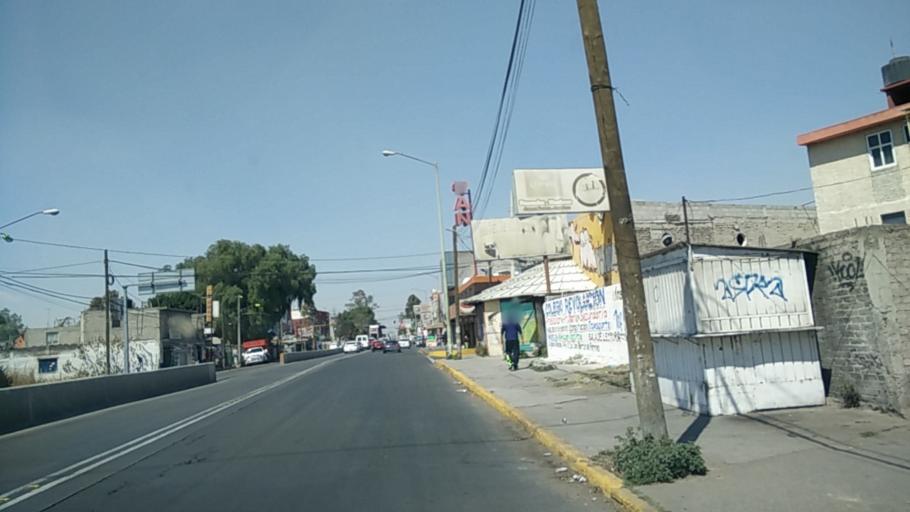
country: MX
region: Mexico
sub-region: Atenco
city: Colonia el Salado
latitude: 19.5943
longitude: -99.0297
